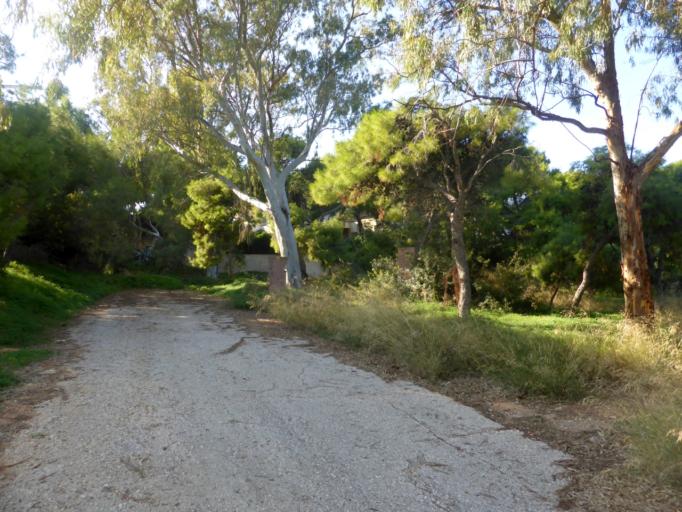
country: GR
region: Attica
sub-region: Nomarchia Anatolikis Attikis
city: Vouliagmeni
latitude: 37.8165
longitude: 23.7654
